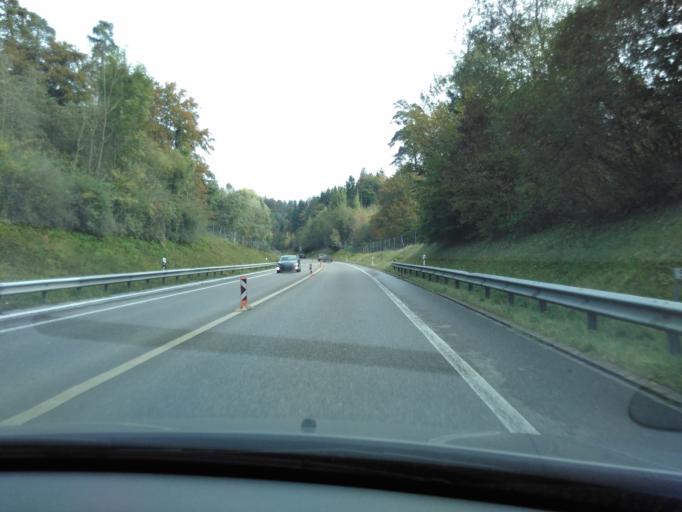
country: CH
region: Zurich
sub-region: Bezirk Hinwil
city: Rueti / Dorfzentrum, Suedl. Teil
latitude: 47.2448
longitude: 8.8534
